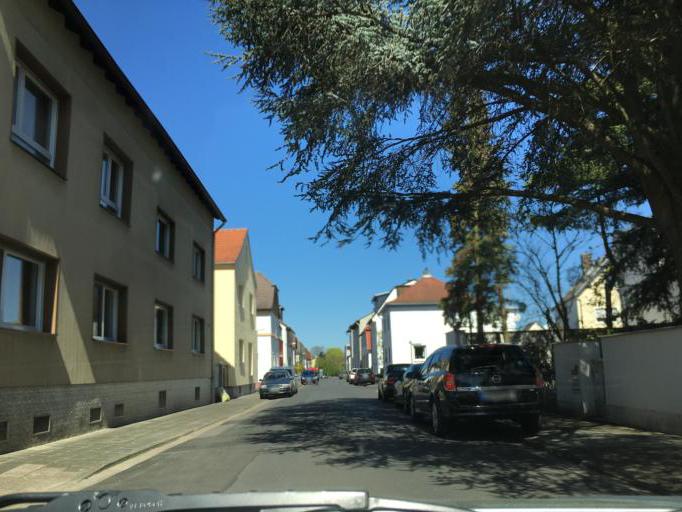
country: DE
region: Hesse
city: Dreieich
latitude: 50.0219
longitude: 8.6934
